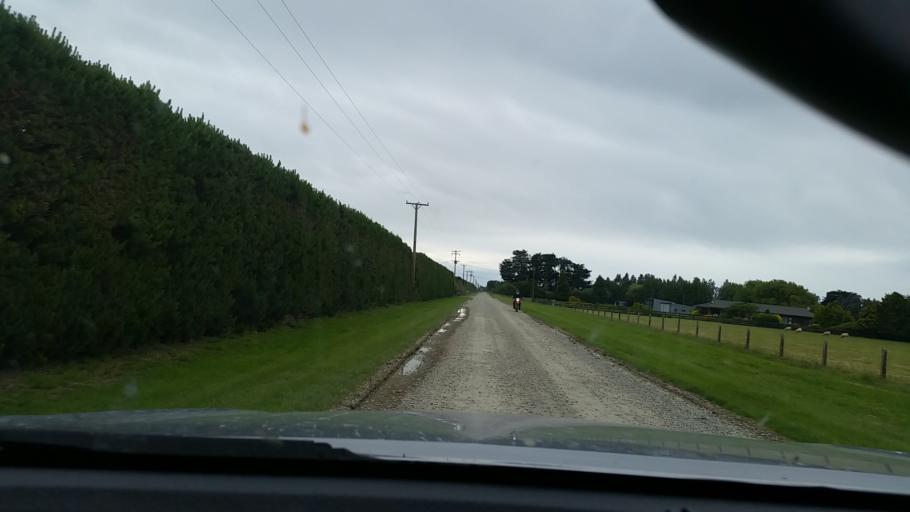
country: NZ
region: Southland
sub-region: Southland District
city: Winton
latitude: -46.2710
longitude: 168.3674
